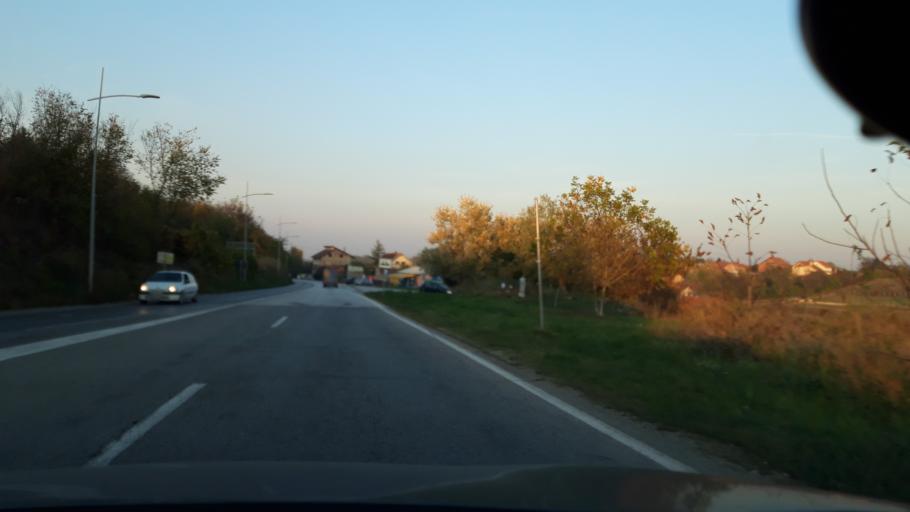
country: RS
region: Autonomna Pokrajina Vojvodina
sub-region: Juznobacki Okrug
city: Petrovaradin
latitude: 45.2249
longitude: 19.8774
